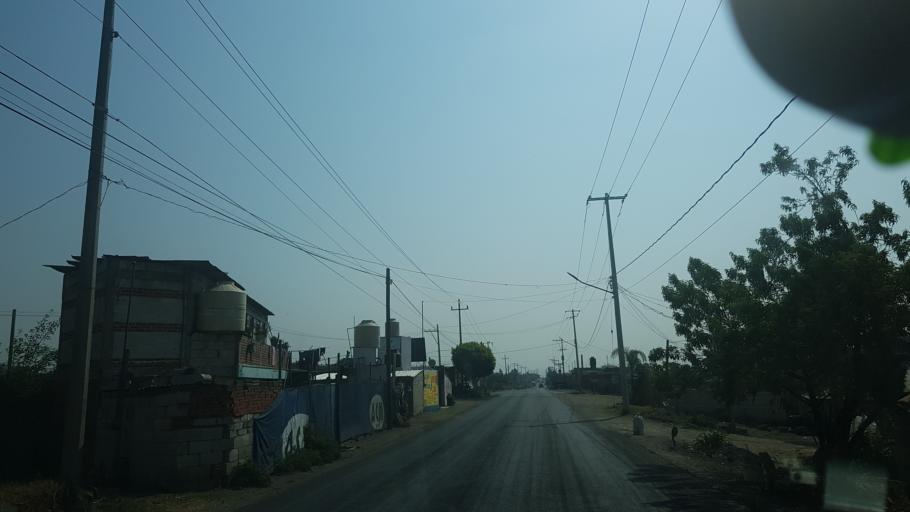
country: MX
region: Puebla
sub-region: San Jeronimo Tecuanipan
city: Los Reyes Tlanechicolpan
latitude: 19.0527
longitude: -98.3440
